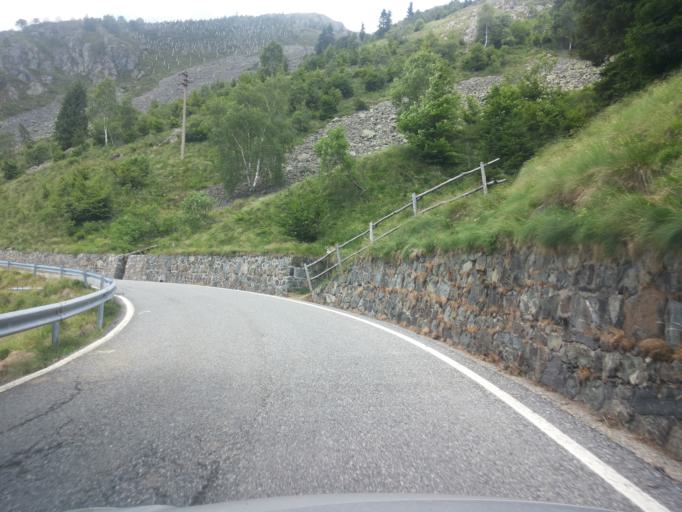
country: IT
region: Piedmont
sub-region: Provincia di Biella
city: Camandona
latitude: 45.6629
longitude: 8.0966
